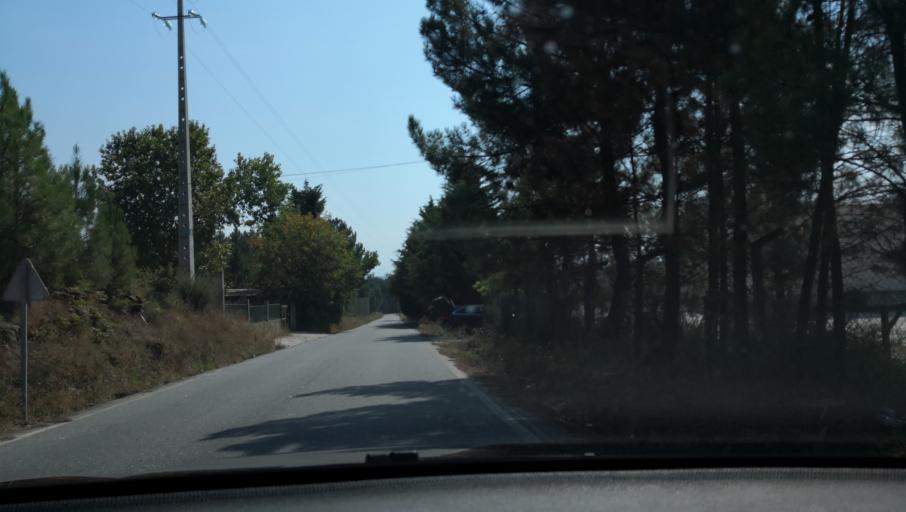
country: PT
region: Vila Real
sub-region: Sabrosa
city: Sabrosa
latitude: 41.3487
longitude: -7.5980
